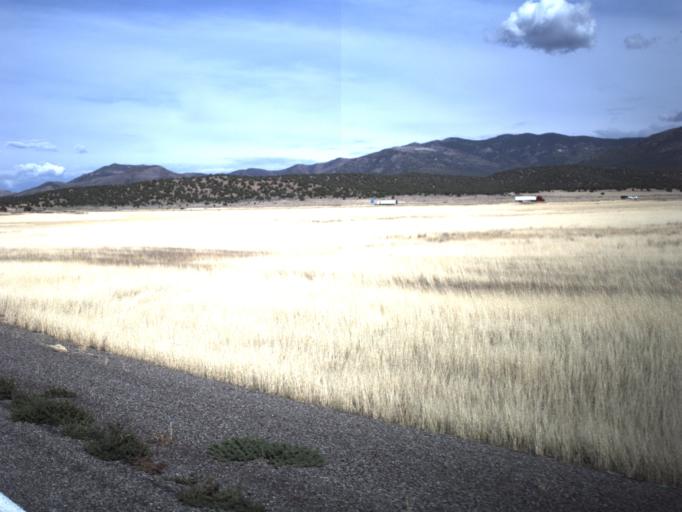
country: US
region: Utah
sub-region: Millard County
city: Fillmore
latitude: 39.1298
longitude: -112.2509
